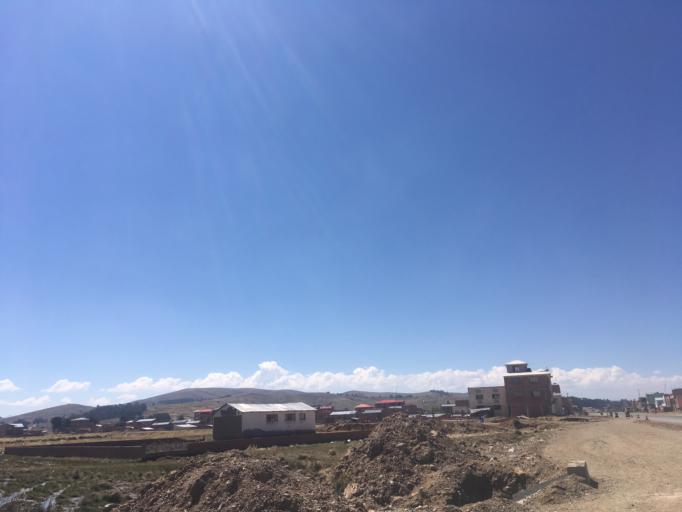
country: BO
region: La Paz
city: Huatajata
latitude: -16.1896
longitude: -68.7472
